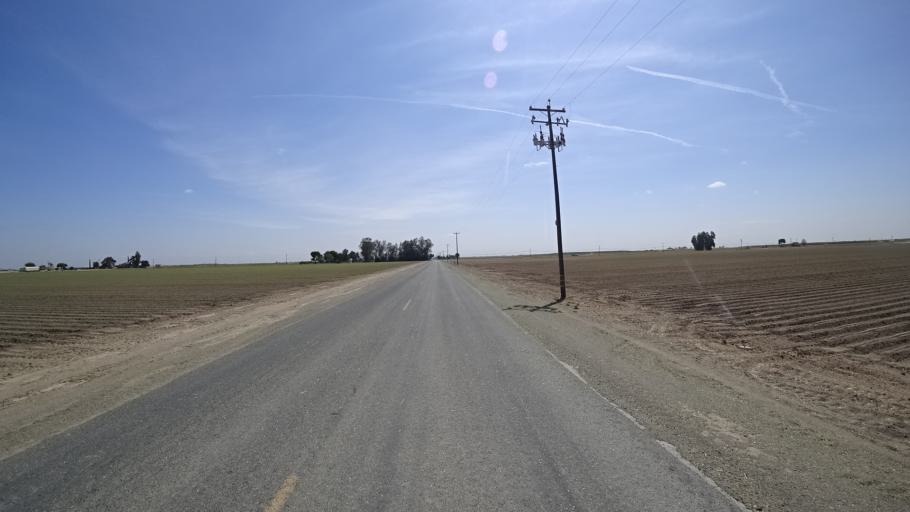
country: US
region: California
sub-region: Kings County
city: Home Garden
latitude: 36.2694
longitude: -119.6232
